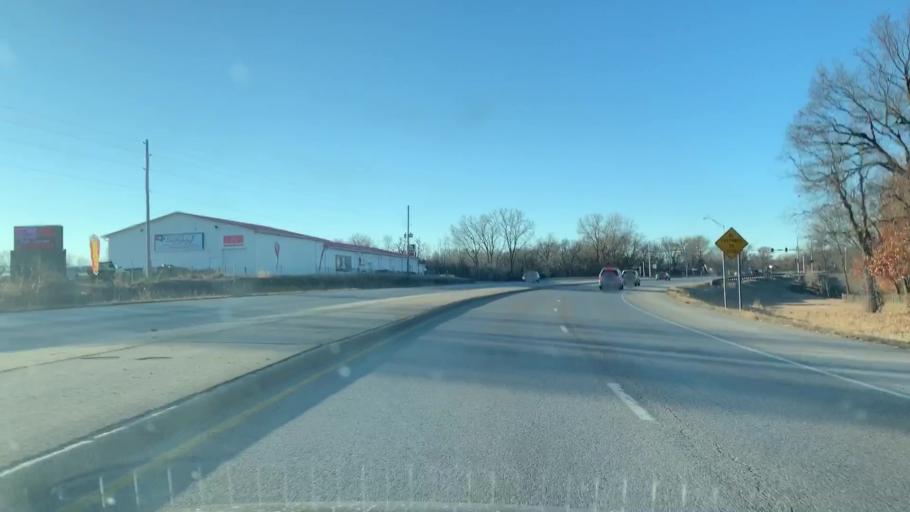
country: US
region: Kansas
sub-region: Bourbon County
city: Fort Scott
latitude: 37.8294
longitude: -94.7021
